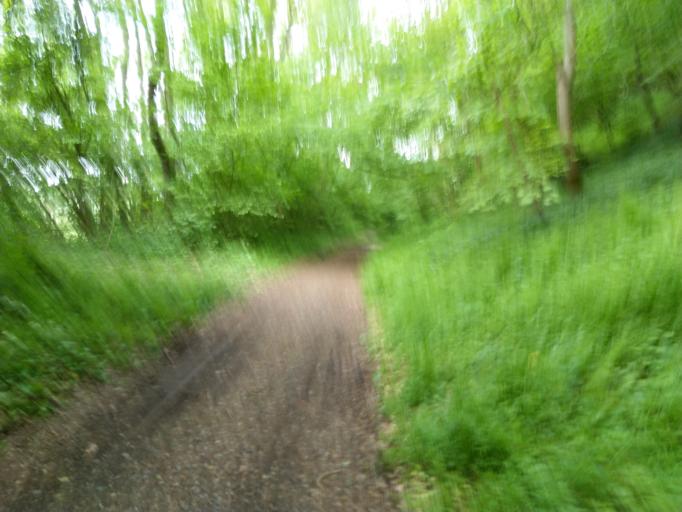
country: FR
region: Picardie
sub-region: Departement de l'Aisne
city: Guise
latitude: 49.9247
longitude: 3.5827
